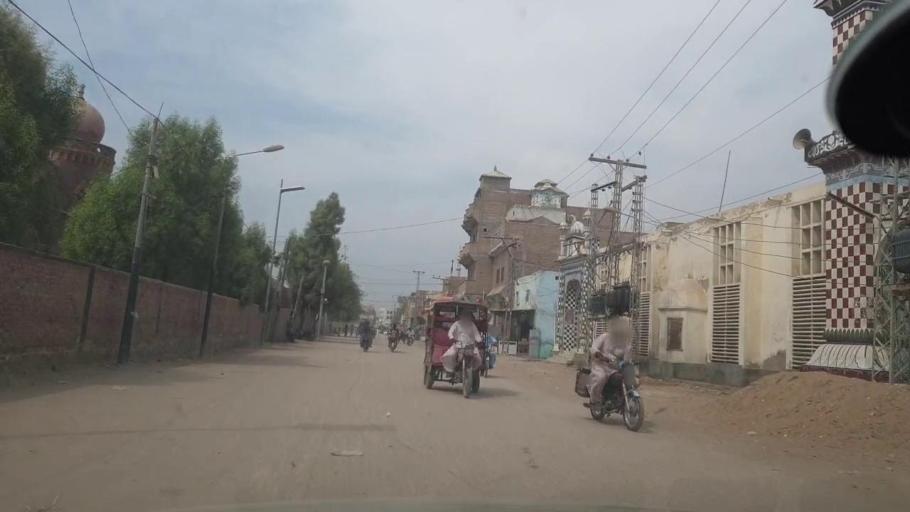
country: PK
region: Sindh
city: Jacobabad
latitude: 28.2751
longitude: 68.4381
